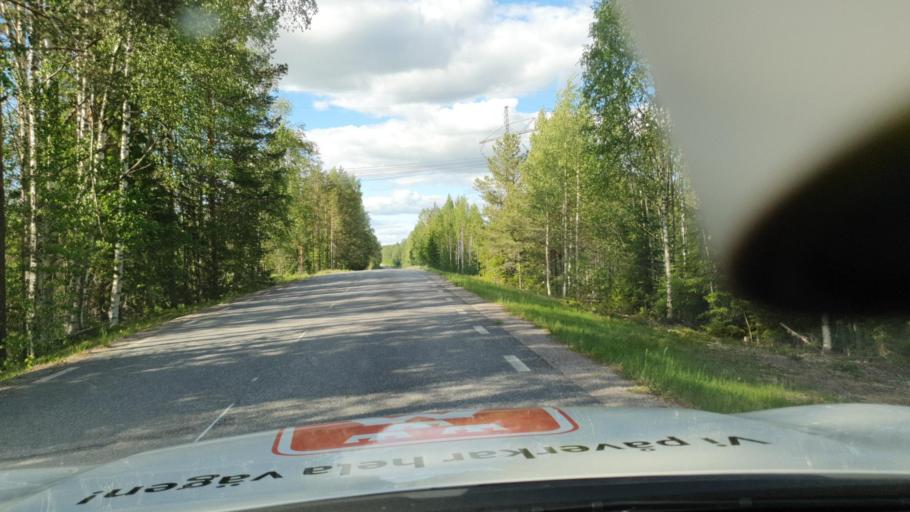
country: SE
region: Vaesterbotten
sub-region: Vannas Kommun
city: Vannasby
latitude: 63.8103
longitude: 19.8559
